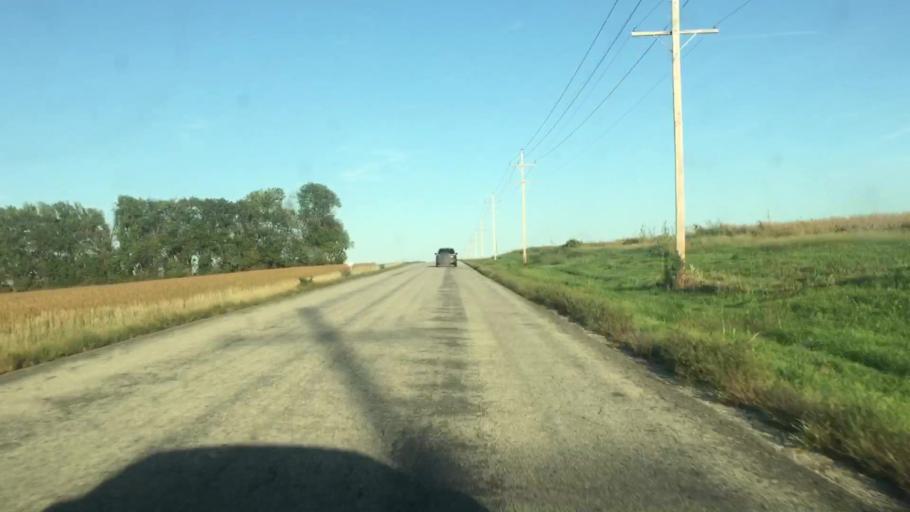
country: US
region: Kansas
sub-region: Atchison County
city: Atchison
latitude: 39.5656
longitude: -95.3228
